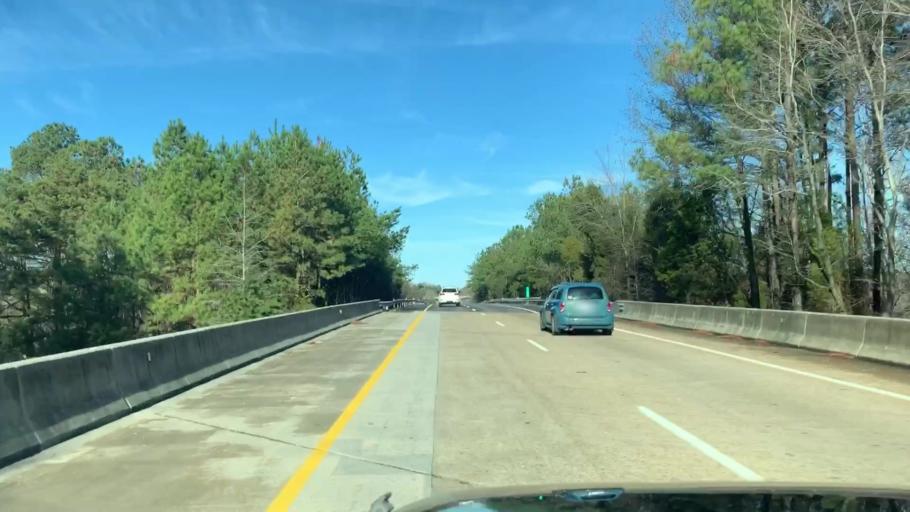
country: US
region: Virginia
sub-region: Henrico County
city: Sandston
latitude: 37.5228
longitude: -77.2680
